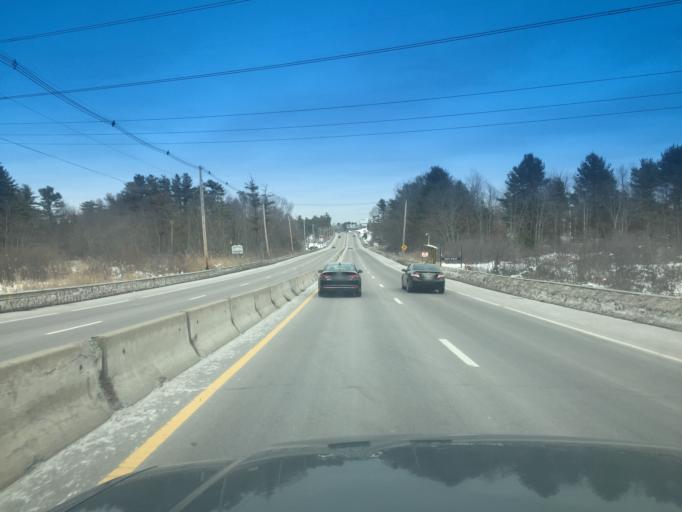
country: US
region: Massachusetts
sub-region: Norfolk County
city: Walpole
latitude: 42.1147
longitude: -71.2397
